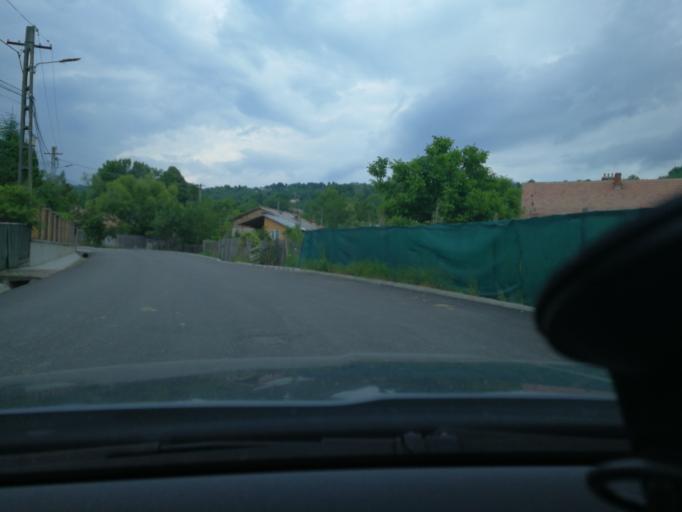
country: RO
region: Prahova
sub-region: Comuna Cornu
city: Cornu de Jos
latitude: 45.1555
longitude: 25.7112
